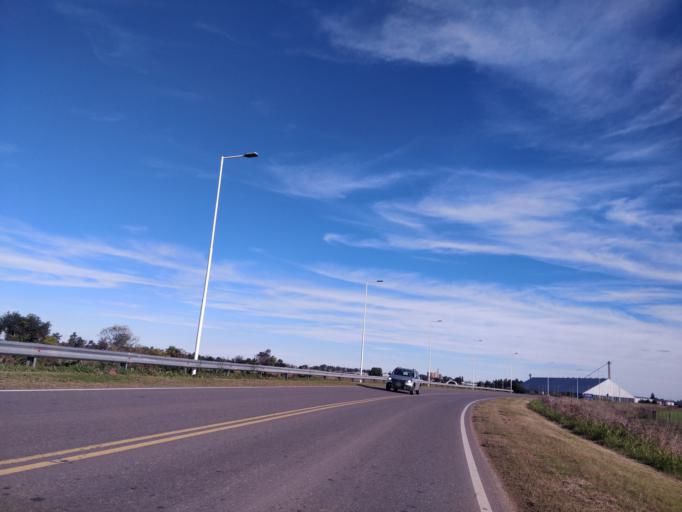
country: AR
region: Cordoba
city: Leones
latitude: -32.6464
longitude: -62.2915
